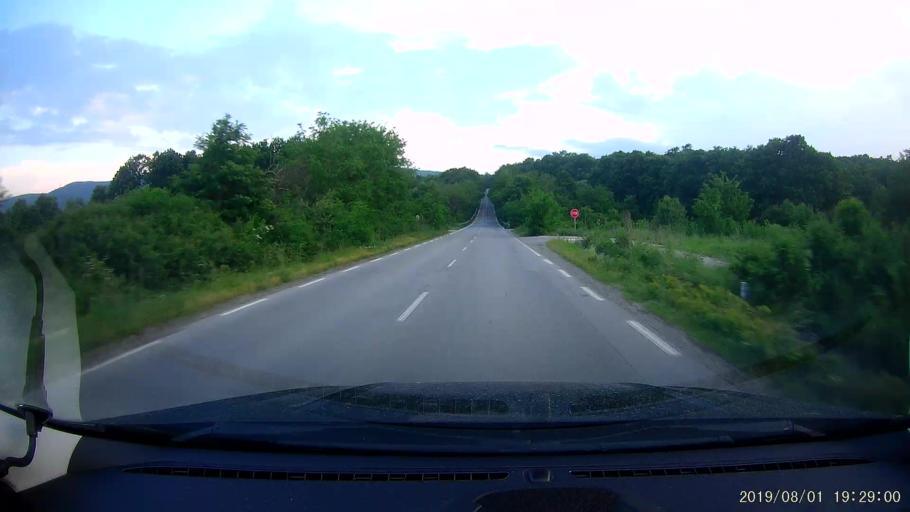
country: BG
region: Burgas
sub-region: Obshtina Sungurlare
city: Sungurlare
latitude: 42.8334
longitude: 26.9116
